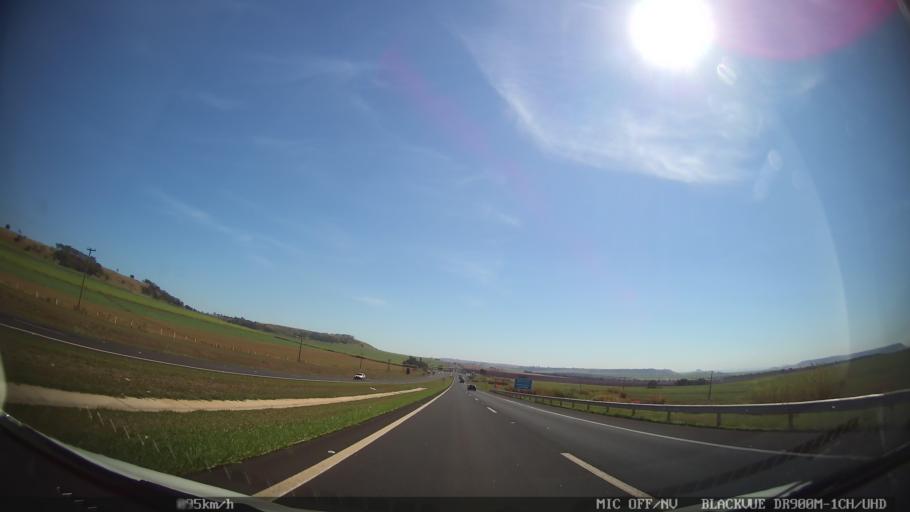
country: BR
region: Sao Paulo
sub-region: Cravinhos
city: Cravinhos
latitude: -21.4203
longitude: -47.6596
